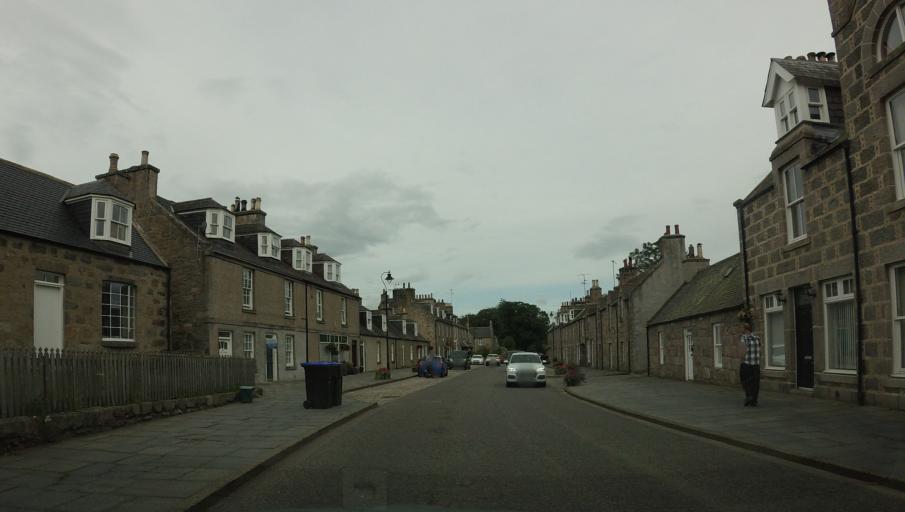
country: GB
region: Scotland
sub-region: Aberdeenshire
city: Torphins
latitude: 57.0865
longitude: -2.6768
